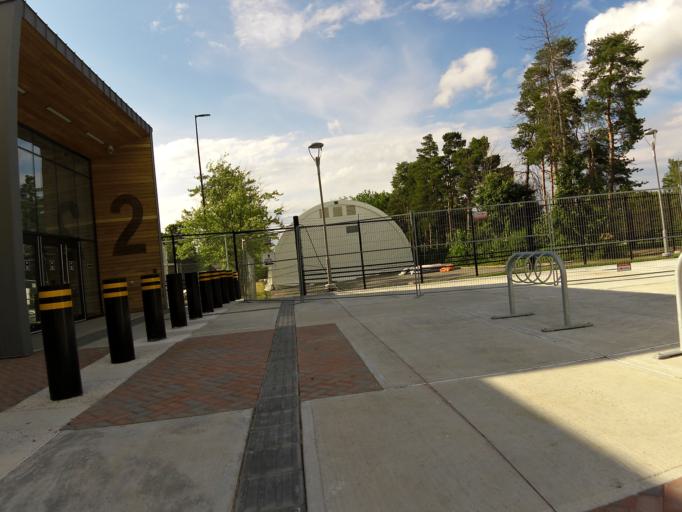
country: CA
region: Ontario
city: Bells Corners
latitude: 45.3505
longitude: -75.8482
